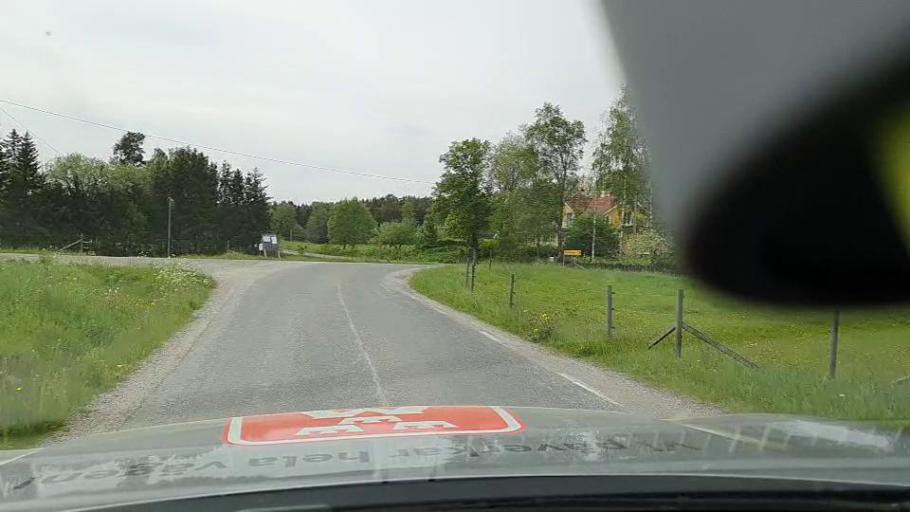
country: SE
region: Soedermanland
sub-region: Flens Kommun
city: Halleforsnas
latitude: 59.1033
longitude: 16.5308
